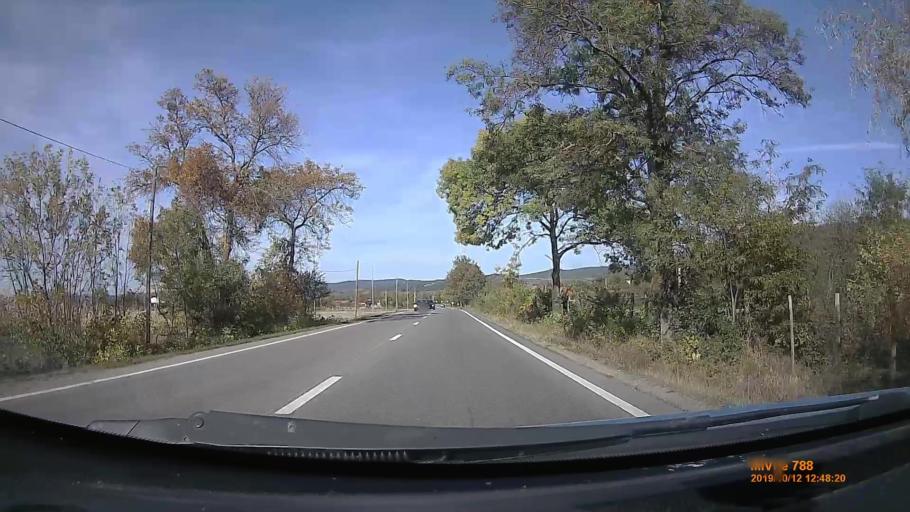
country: RO
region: Bihor
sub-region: Comuna Vadu Crisului
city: Vadu Crisului
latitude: 47.0098
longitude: 22.5179
